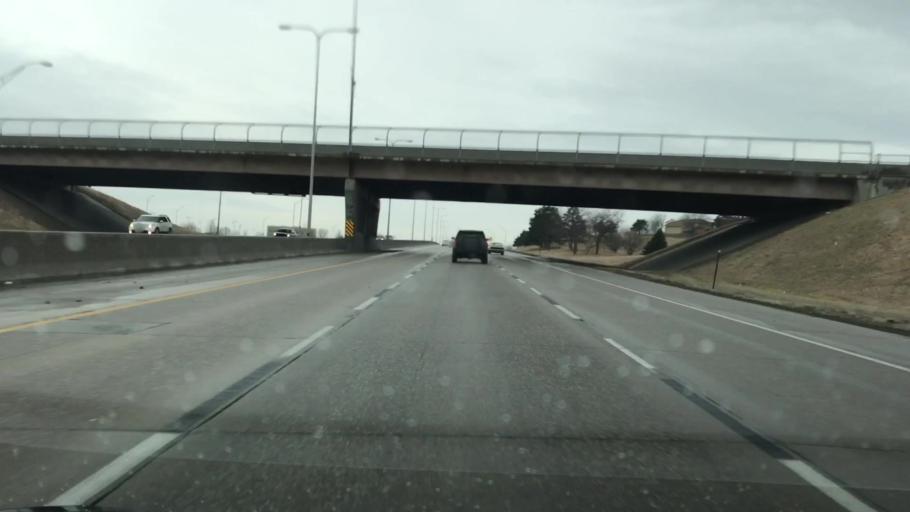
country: US
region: Nebraska
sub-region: Sarpy County
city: Chalco
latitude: 41.1857
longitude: -96.1085
